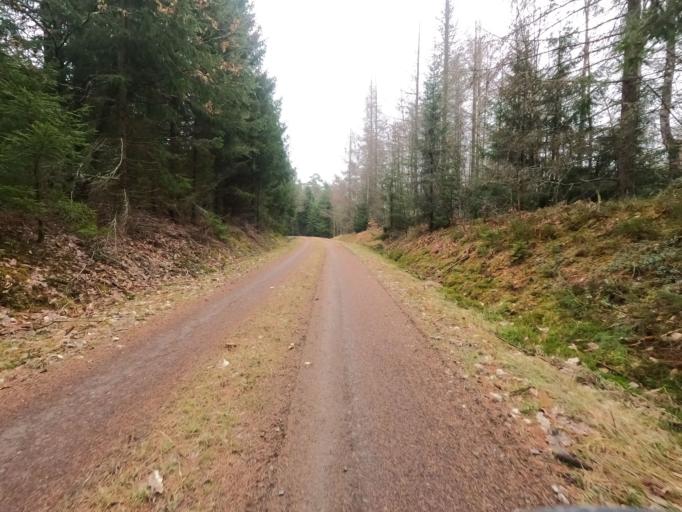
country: SE
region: Kronoberg
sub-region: Markaryds Kommun
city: Stromsnasbruk
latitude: 56.7896
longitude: 13.6296
